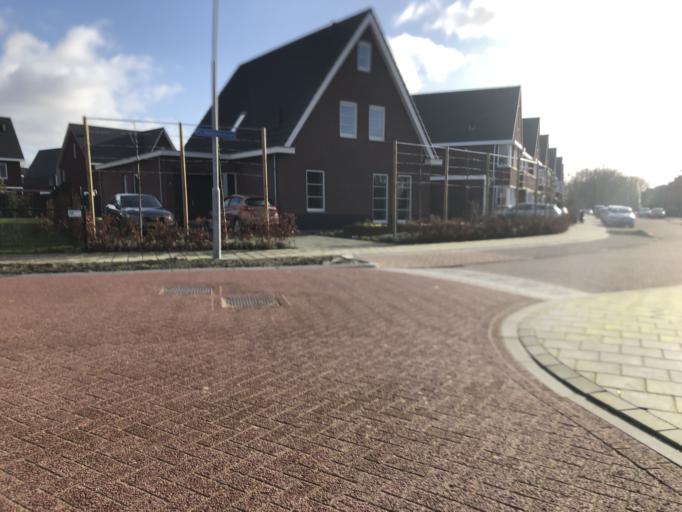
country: NL
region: Zeeland
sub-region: Gemeente Middelburg
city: Middelburg
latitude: 51.4881
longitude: 3.5937
